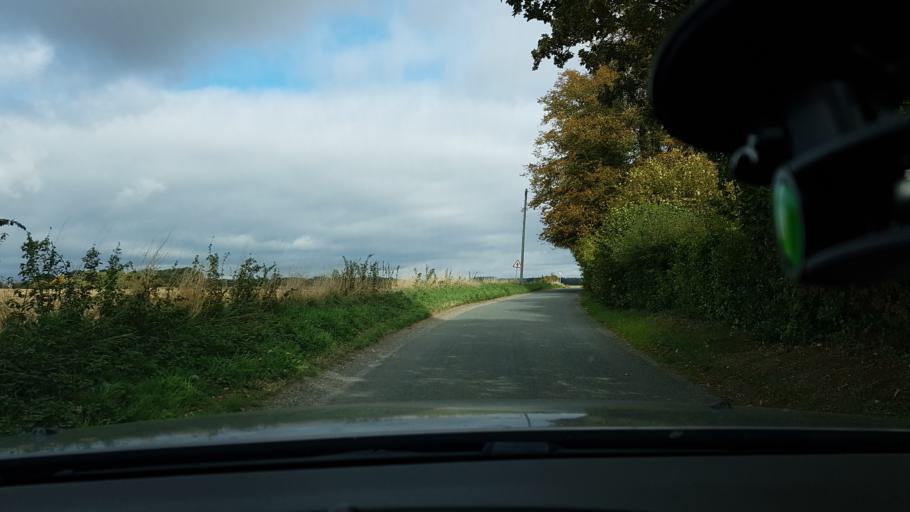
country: GB
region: England
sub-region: Wiltshire
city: Great Bedwyn
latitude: 51.3932
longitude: -1.5879
